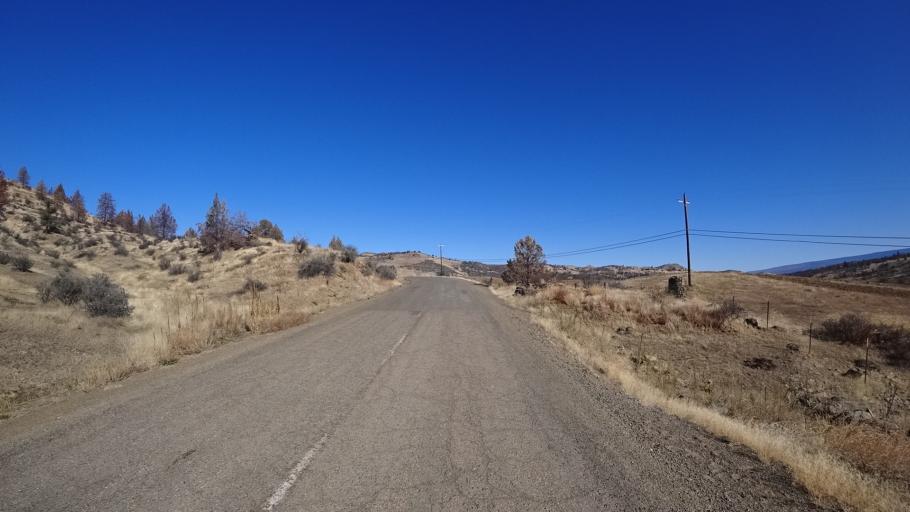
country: US
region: California
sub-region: Siskiyou County
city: Montague
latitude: 41.8900
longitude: -122.5501
